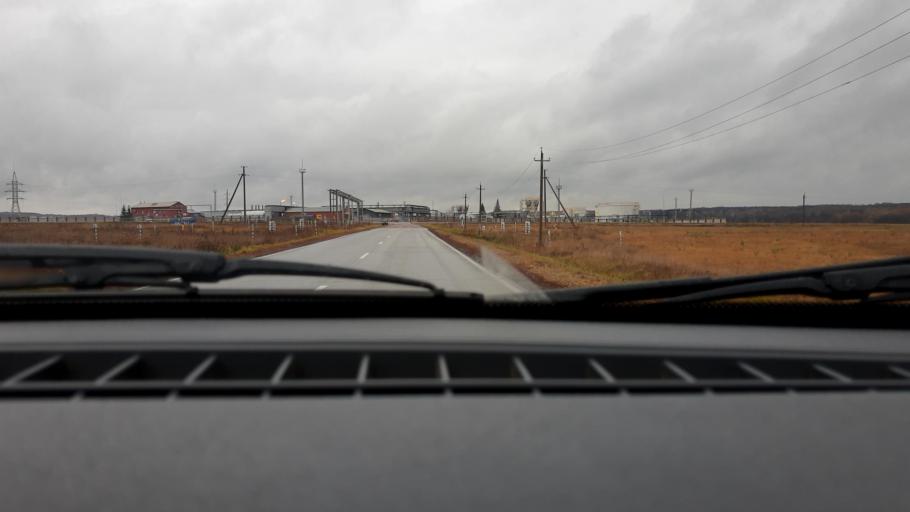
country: RU
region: Bashkortostan
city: Mikhaylovka
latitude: 54.8211
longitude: 55.7661
